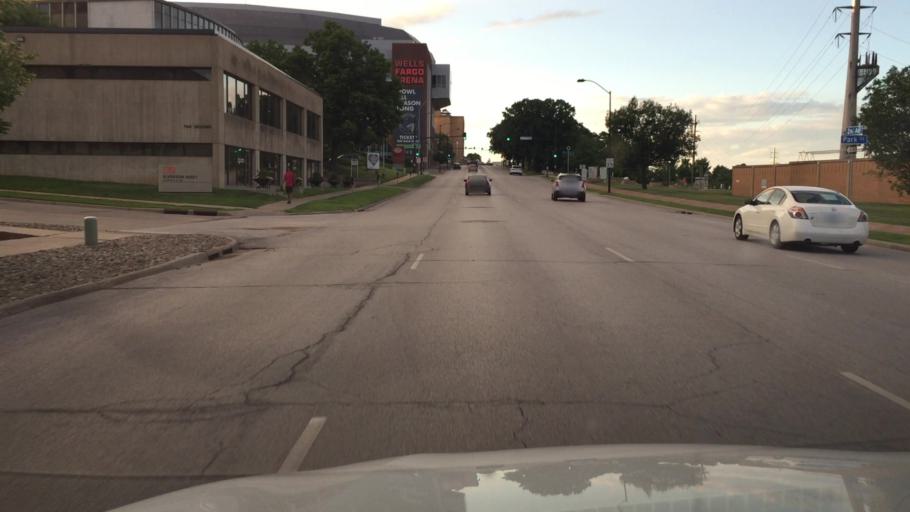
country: US
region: Iowa
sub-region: Polk County
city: Des Moines
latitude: 41.5903
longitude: -93.6204
